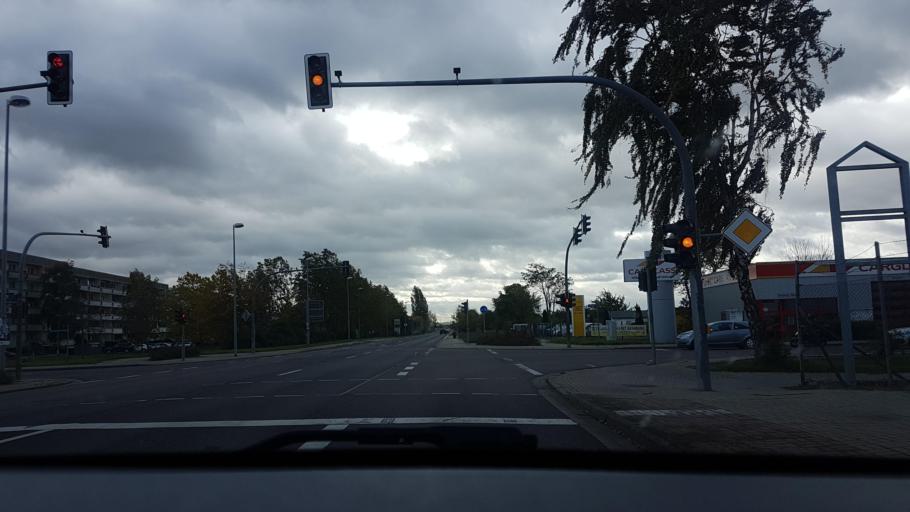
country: DE
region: Saxony-Anhalt
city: Bernburg
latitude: 51.7776
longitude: 11.7475
